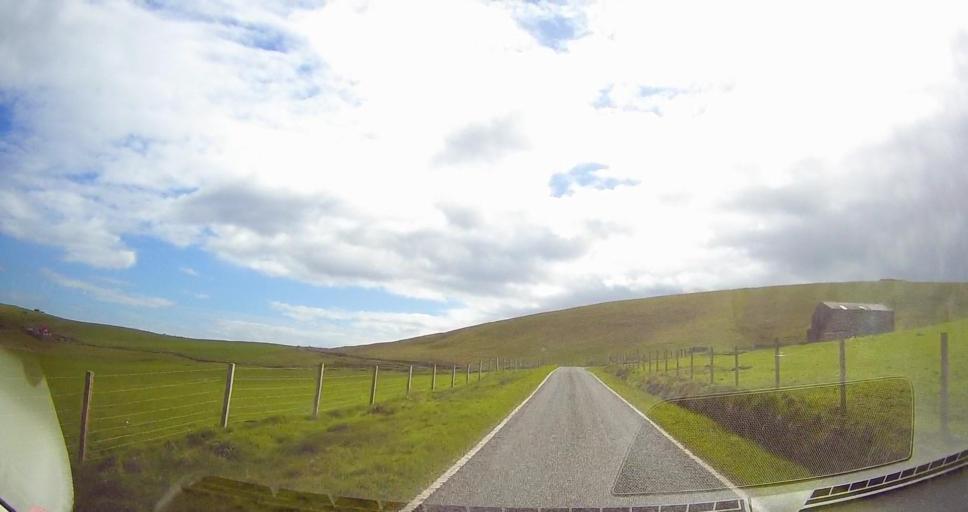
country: GB
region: Scotland
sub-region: Shetland Islands
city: Sandwick
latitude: 59.9286
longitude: -1.3453
